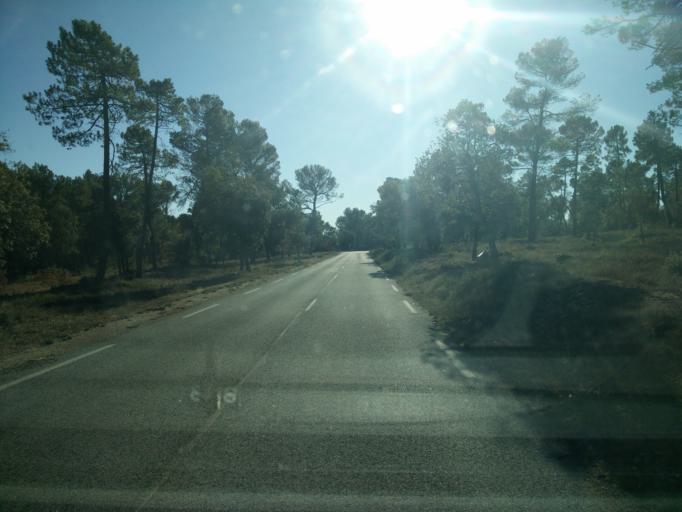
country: FR
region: Provence-Alpes-Cote d'Azur
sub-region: Departement du Var
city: Salernes
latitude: 43.5866
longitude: 6.2262
